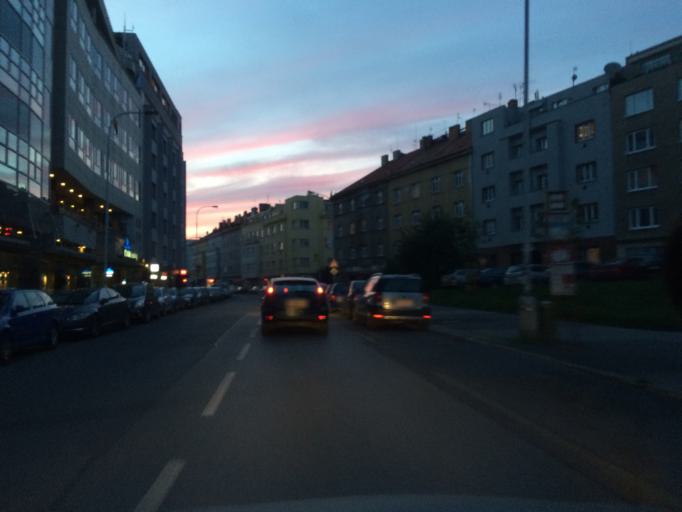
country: CZ
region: Praha
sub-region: Praha 2
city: Vysehrad
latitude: 50.0571
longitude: 14.4341
